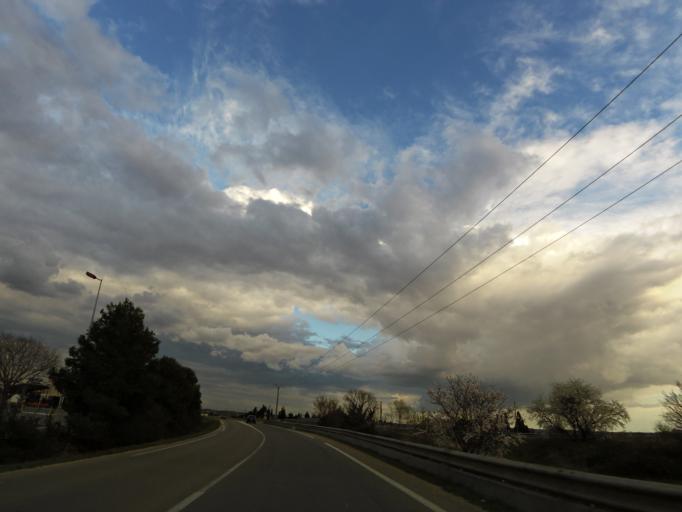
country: FR
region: Languedoc-Roussillon
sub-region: Departement du Gard
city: Codognan
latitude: 43.7265
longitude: 4.2424
